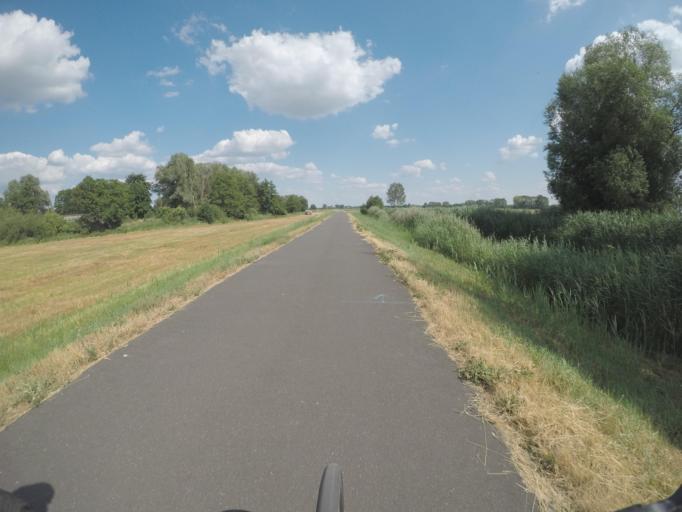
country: DE
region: Brandenburg
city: Ketzin
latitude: 52.4622
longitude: 12.8514
